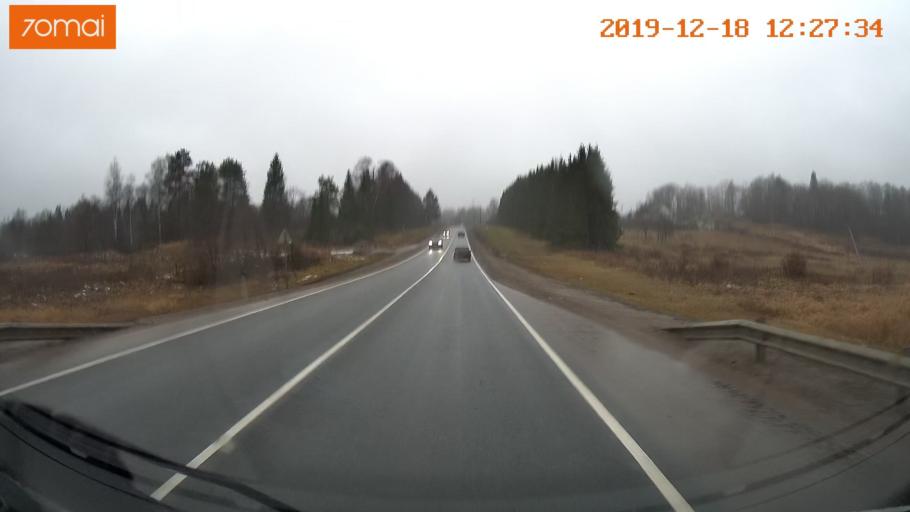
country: RU
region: Moskovskaya
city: Novopetrovskoye
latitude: 56.0642
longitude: 36.5020
